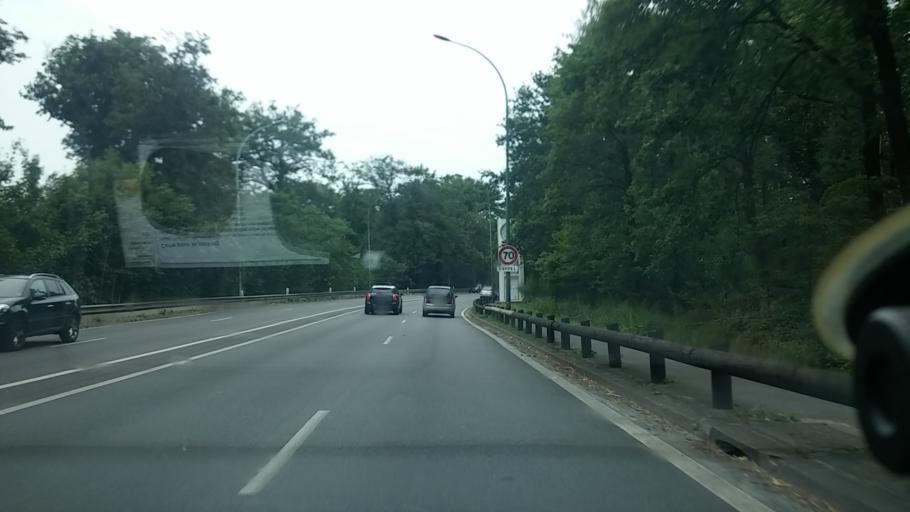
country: FR
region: Ile-de-France
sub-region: Departement des Hauts-de-Seine
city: Vaucresson
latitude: 48.8224
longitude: 2.1514
